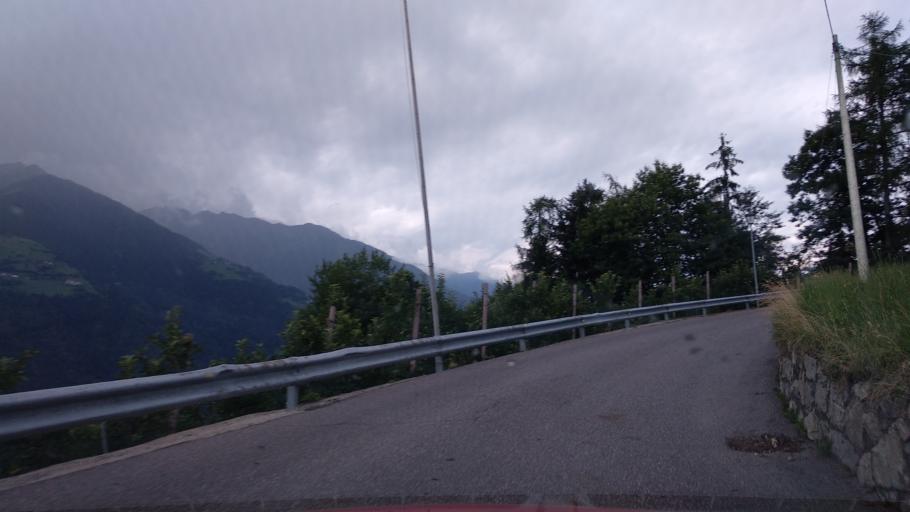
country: IT
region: Trentino-Alto Adige
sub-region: Bolzano
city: Scena
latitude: 46.6946
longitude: 11.1979
